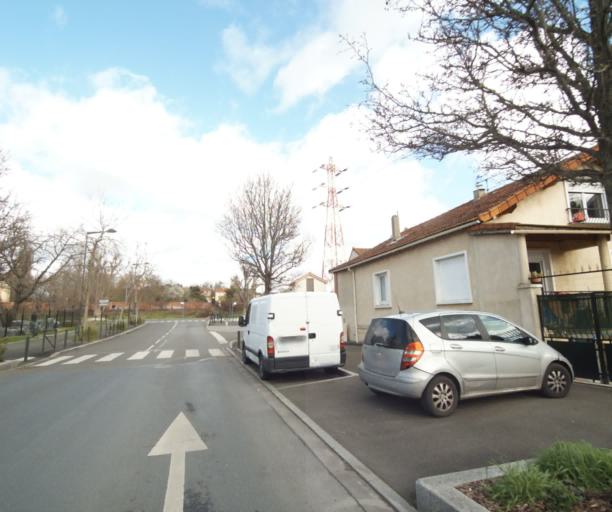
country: FR
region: Ile-de-France
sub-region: Departement de Seine-Saint-Denis
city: Villetaneuse
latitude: 48.9594
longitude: 2.3504
